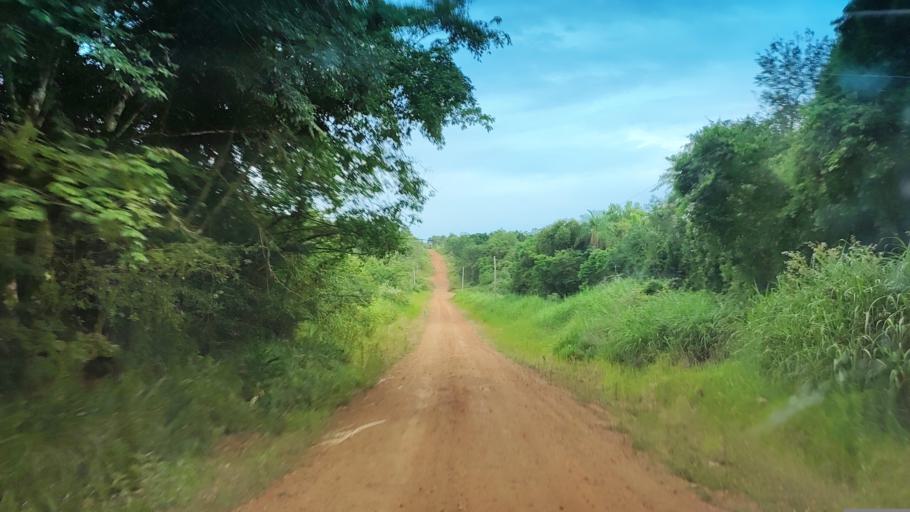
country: AR
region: Misiones
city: Gobernador Roca
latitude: -27.1572
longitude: -55.4648
